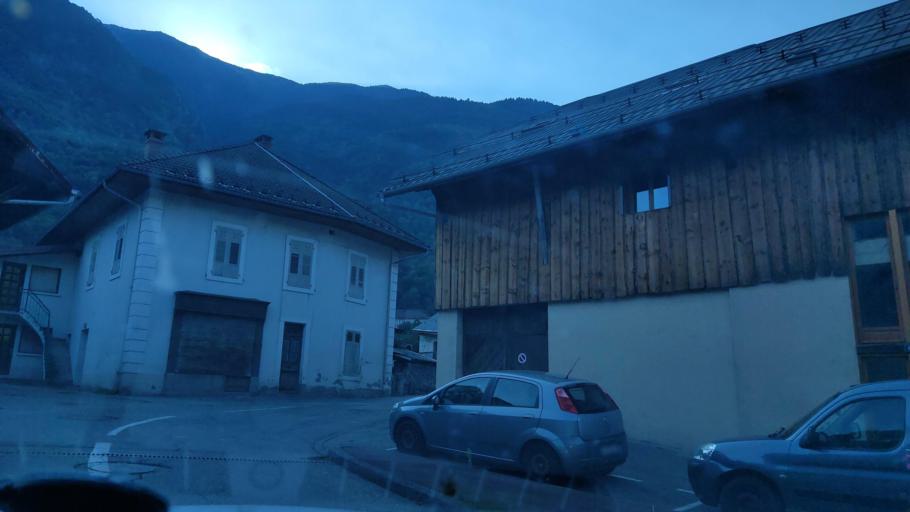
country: FR
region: Rhone-Alpes
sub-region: Departement de la Savoie
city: La Bathie
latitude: 45.5915
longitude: 6.4527
